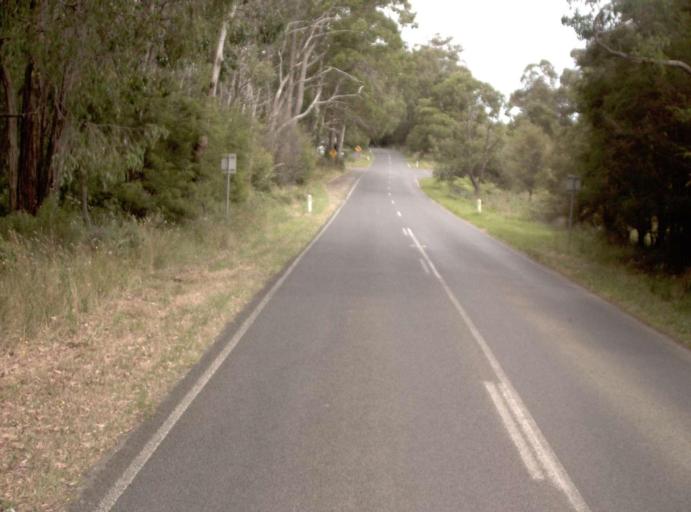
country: AU
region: Victoria
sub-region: Latrobe
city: Traralgon
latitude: -38.1279
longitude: 146.4720
